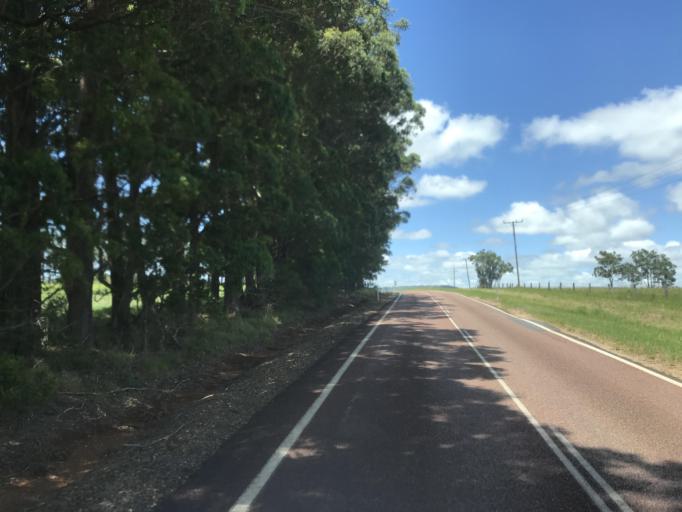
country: AU
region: Queensland
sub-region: Tablelands
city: Ravenshoe
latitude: -17.5301
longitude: 145.4536
